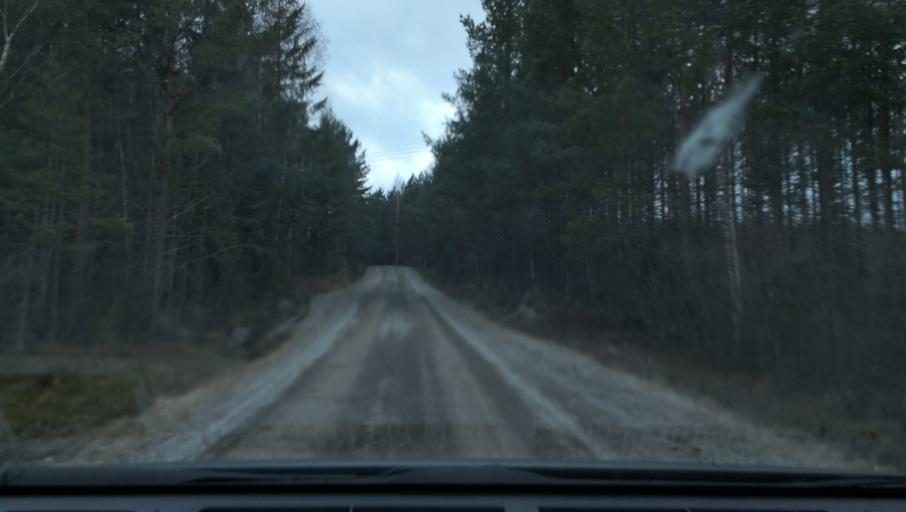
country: SE
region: Vaestmanland
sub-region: Kopings Kommun
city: Kolsva
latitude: 59.5672
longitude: 15.8122
